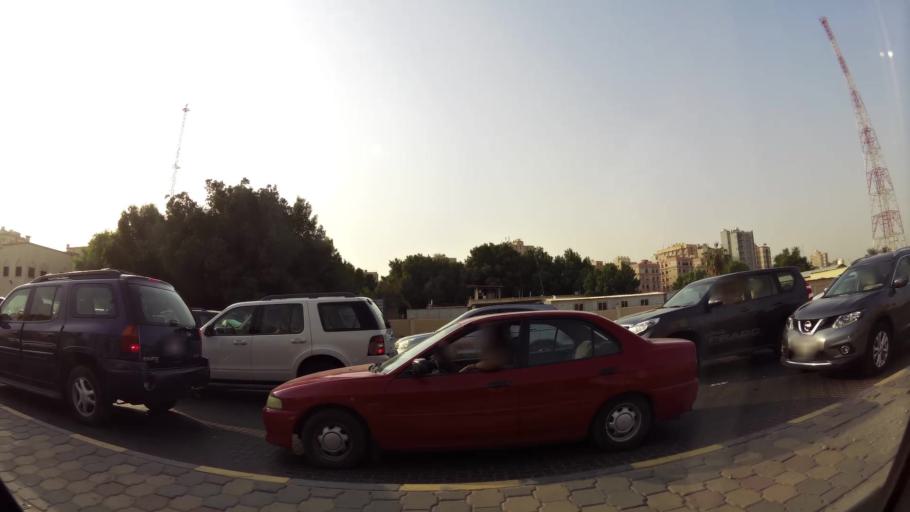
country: KW
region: Muhafazat Hawalli
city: Hawalli
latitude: 29.3326
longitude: 48.0523
